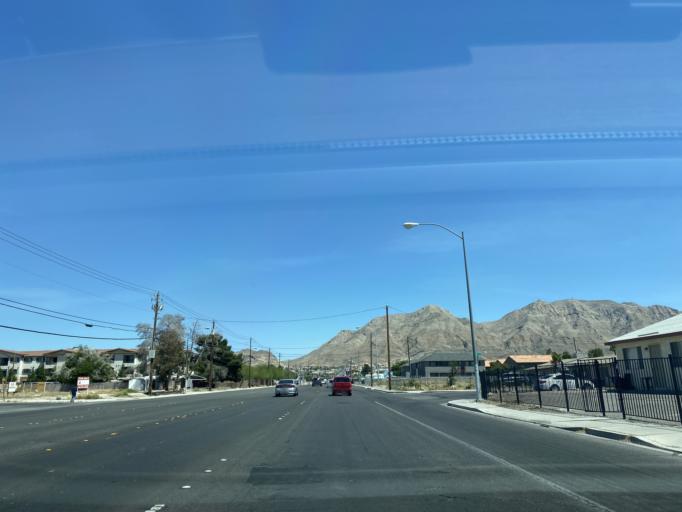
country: US
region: Nevada
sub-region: Clark County
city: Sunrise Manor
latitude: 36.1962
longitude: -115.0489
